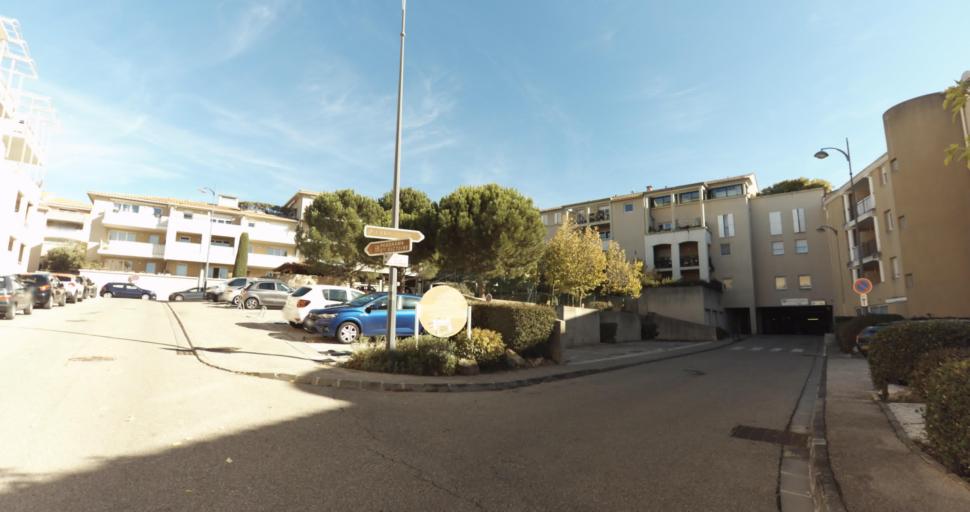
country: FR
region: Provence-Alpes-Cote d'Azur
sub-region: Departement des Bouches-du-Rhone
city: Venelles
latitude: 43.5971
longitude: 5.4797
